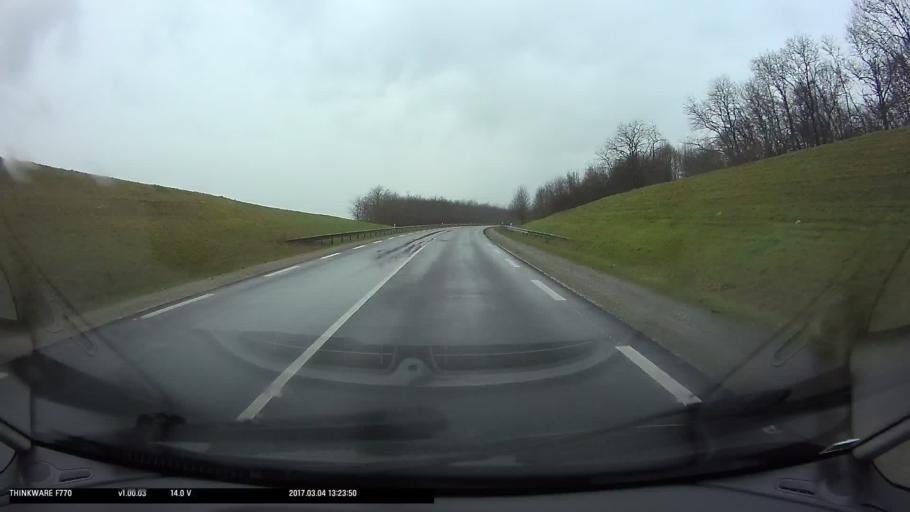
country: FR
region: Ile-de-France
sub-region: Departement du Val-d'Oise
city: Marines
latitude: 49.1350
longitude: 1.9749
